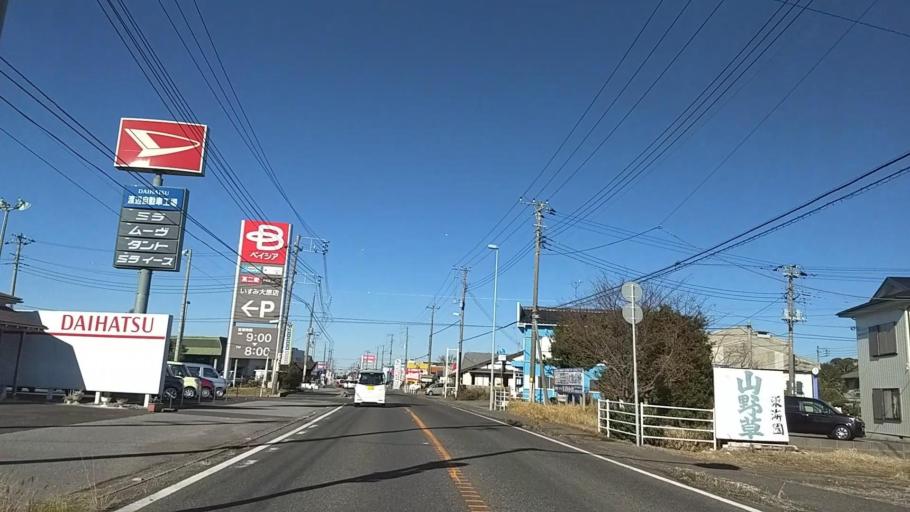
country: JP
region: Chiba
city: Ohara
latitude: 35.2763
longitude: 140.3941
